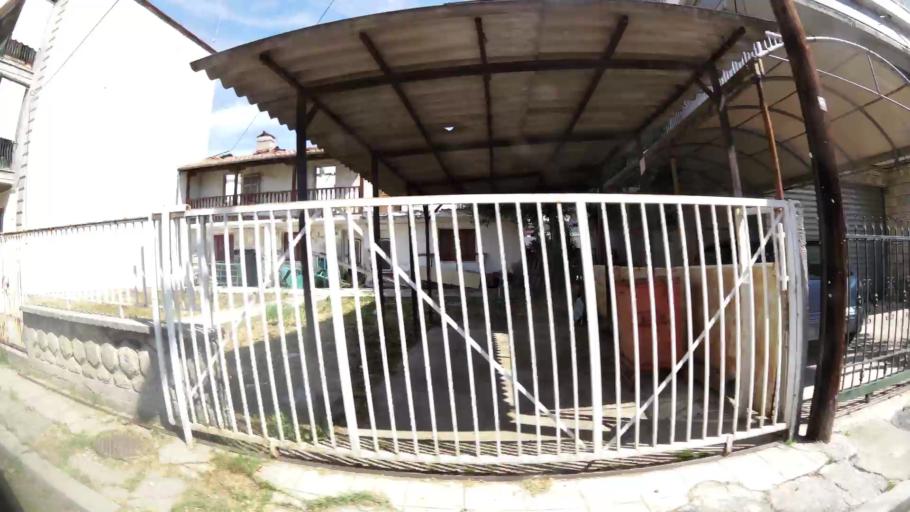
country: GR
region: Central Macedonia
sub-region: Nomos Pierias
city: Katerini
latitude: 40.2710
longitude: 22.4903
